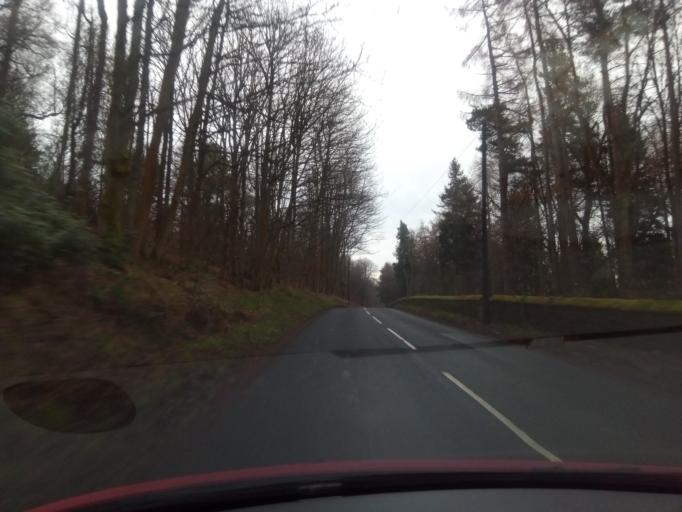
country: GB
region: England
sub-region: Northumberland
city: Whittingham
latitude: 55.4770
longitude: -1.8675
